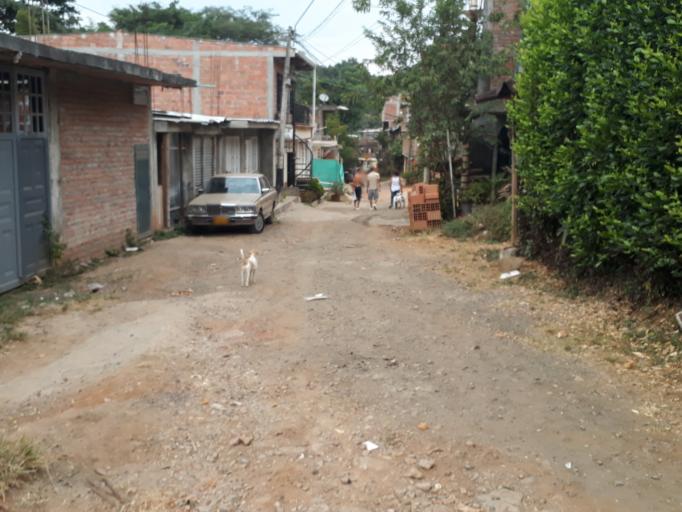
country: CO
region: Valle del Cauca
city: Cali
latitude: 3.4077
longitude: -76.5767
